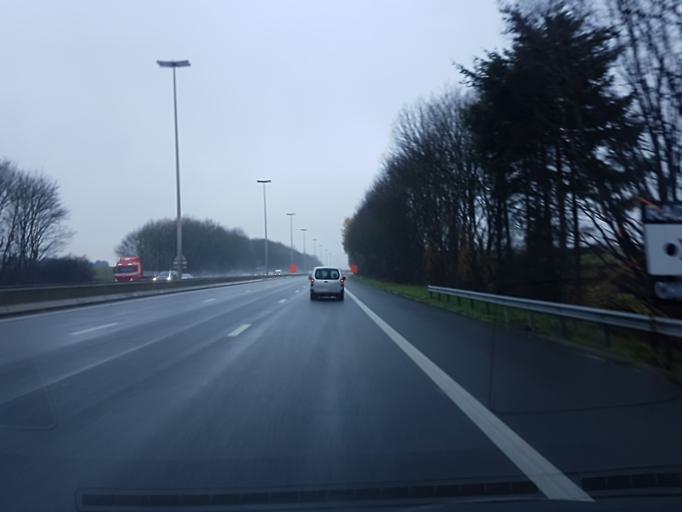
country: BE
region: Wallonia
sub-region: Province de Liege
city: Heron
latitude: 50.5294
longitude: 5.0908
